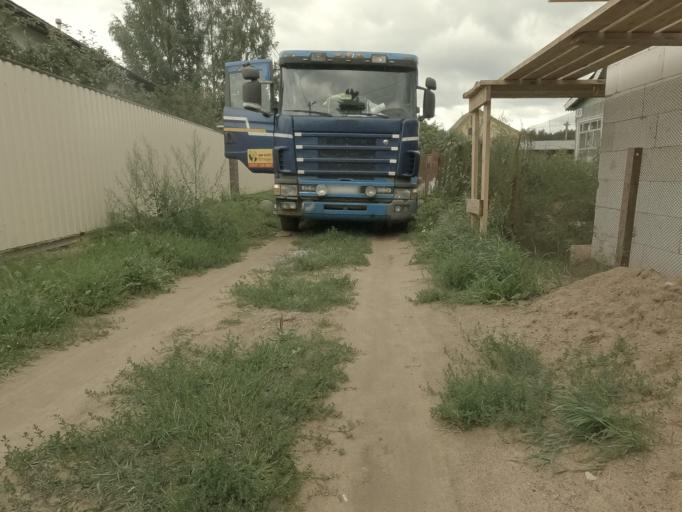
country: RU
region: Leningrad
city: Kirovsk
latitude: 59.8963
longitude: 31.0070
